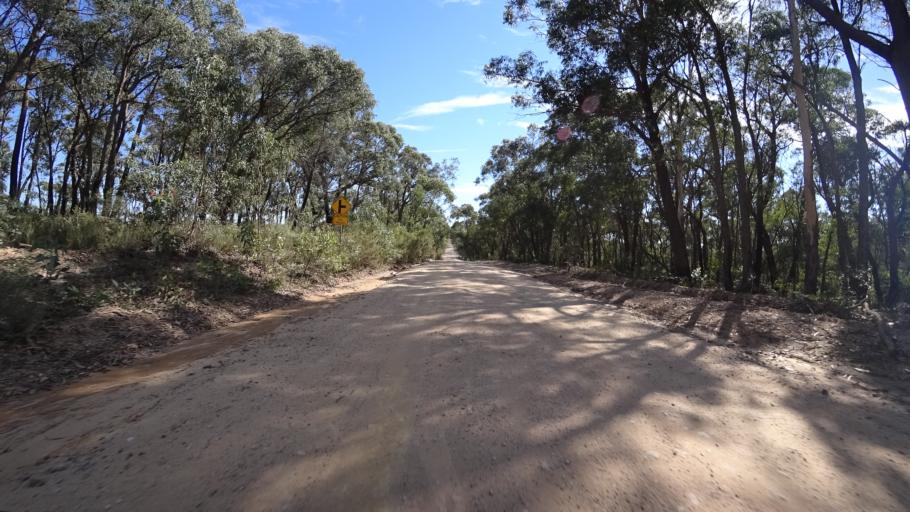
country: AU
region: New South Wales
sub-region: Lithgow
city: Lithgow
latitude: -33.4239
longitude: 150.2017
